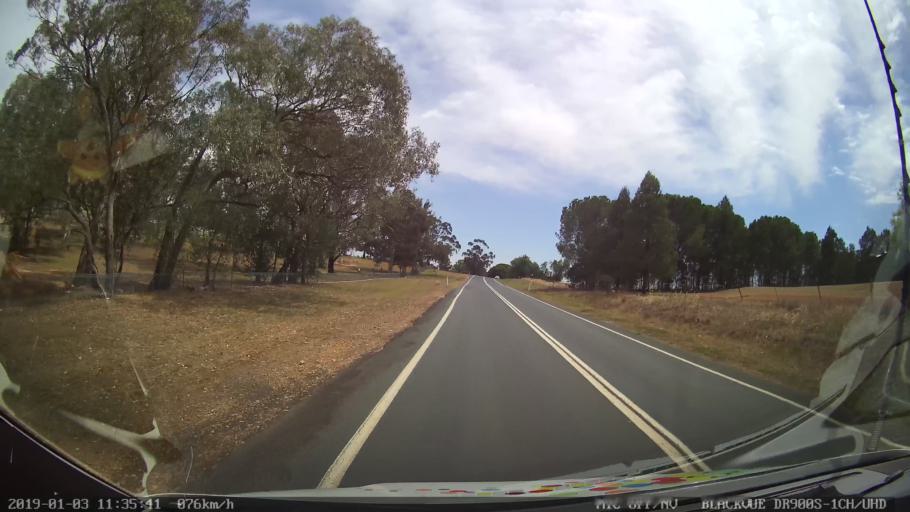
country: AU
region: New South Wales
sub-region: Weddin
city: Grenfell
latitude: -33.9192
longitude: 148.1595
